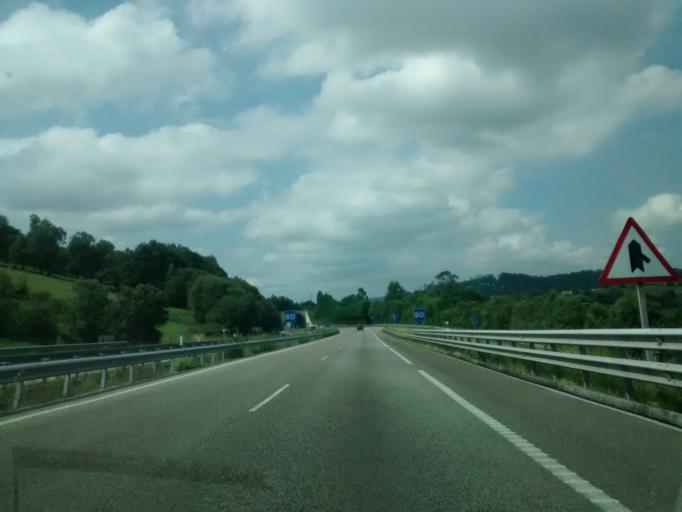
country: ES
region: Asturias
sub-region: Province of Asturias
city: Pola de Siero
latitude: 43.3558
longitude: -5.6811
